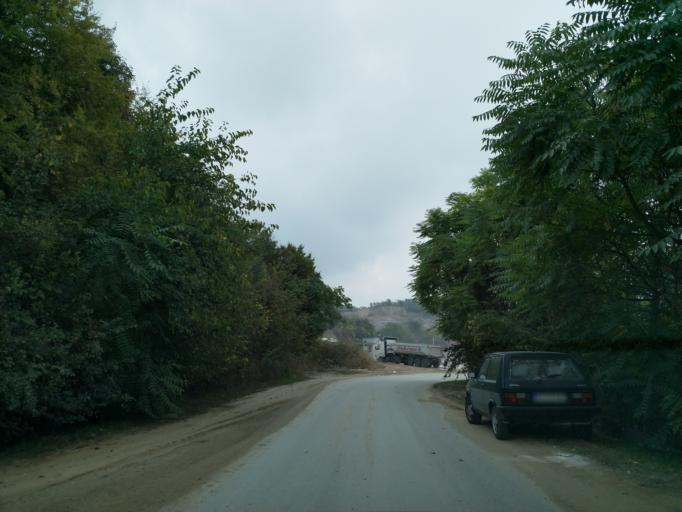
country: RS
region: Central Serbia
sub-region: Sumadijski Okrug
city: Batocina
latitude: 44.1445
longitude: 21.0313
